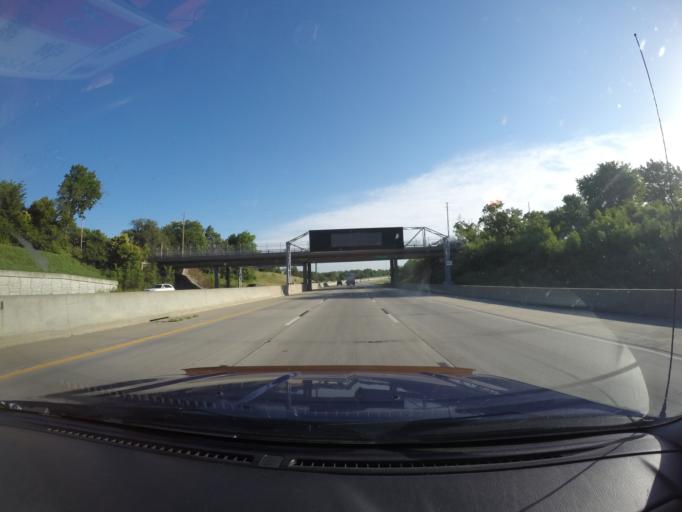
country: US
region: Kansas
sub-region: Wyandotte County
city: Kansas City
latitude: 39.1351
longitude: -94.6760
